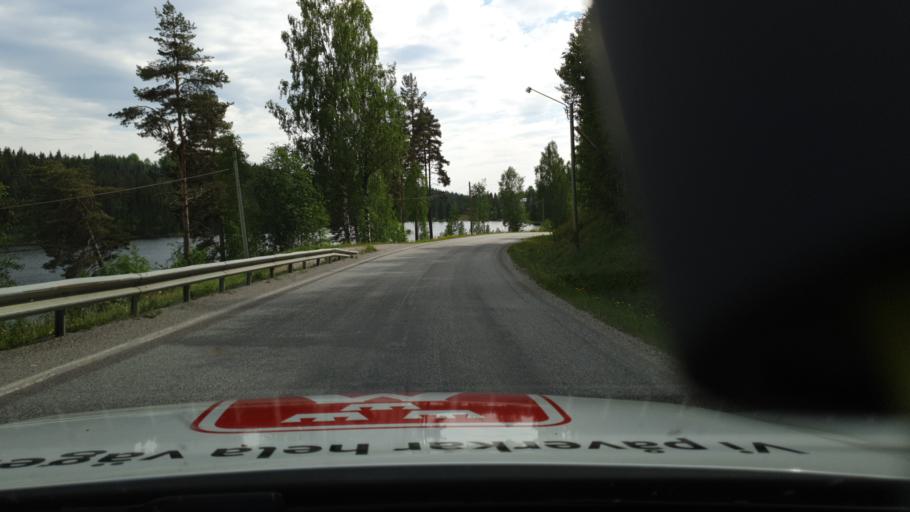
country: SE
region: Jaemtland
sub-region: Braecke Kommun
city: Braecke
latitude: 63.0340
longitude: 15.2497
